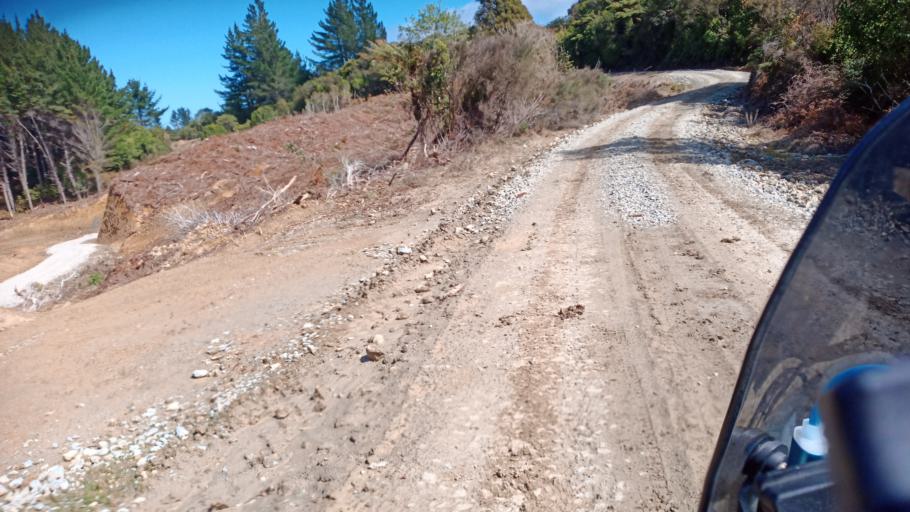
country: NZ
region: Gisborne
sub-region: Gisborne District
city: Gisborne
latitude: -38.8701
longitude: 177.7903
